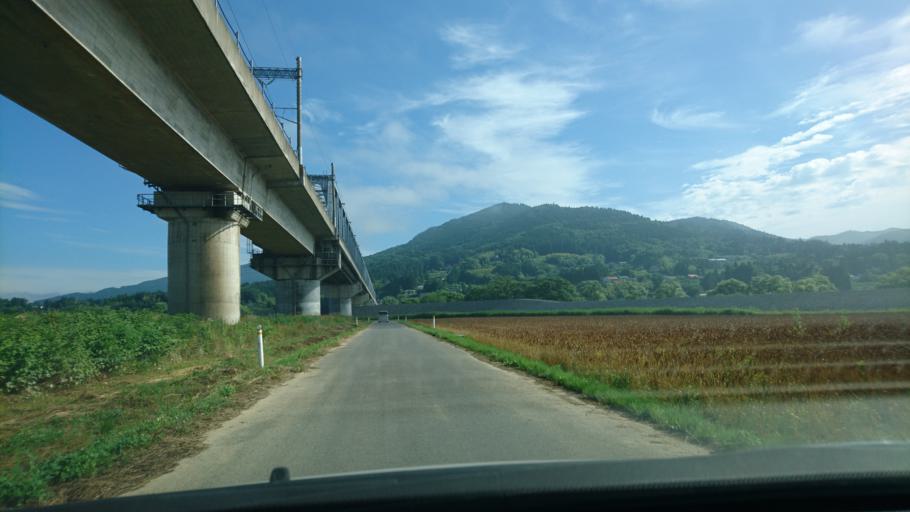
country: JP
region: Iwate
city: Ichinoseki
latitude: 38.9709
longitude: 141.1550
